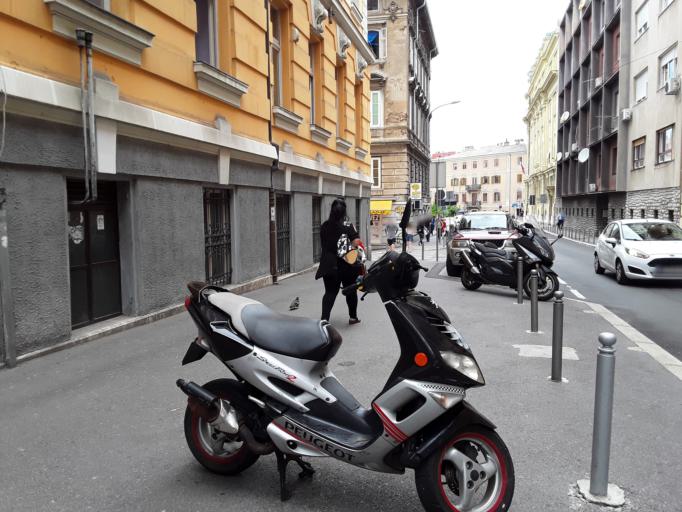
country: HR
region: Primorsko-Goranska
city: Drenova
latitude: 45.3285
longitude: 14.4414
